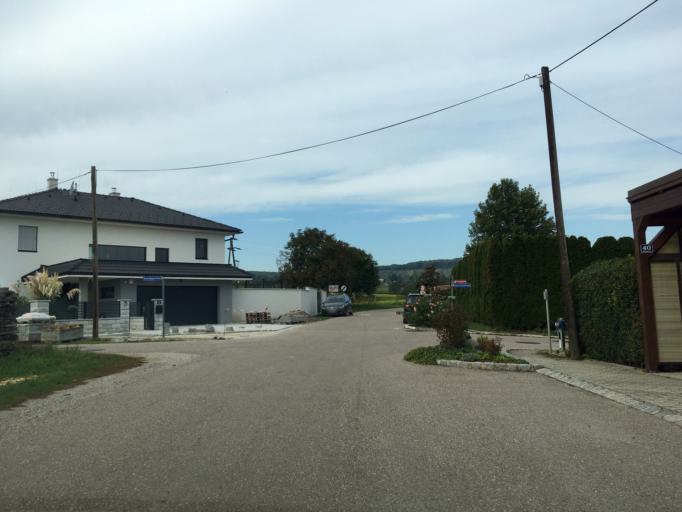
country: AT
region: Burgenland
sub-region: Politischer Bezirk Neusiedl am See
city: Winden am See
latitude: 47.9542
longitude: 16.7483
